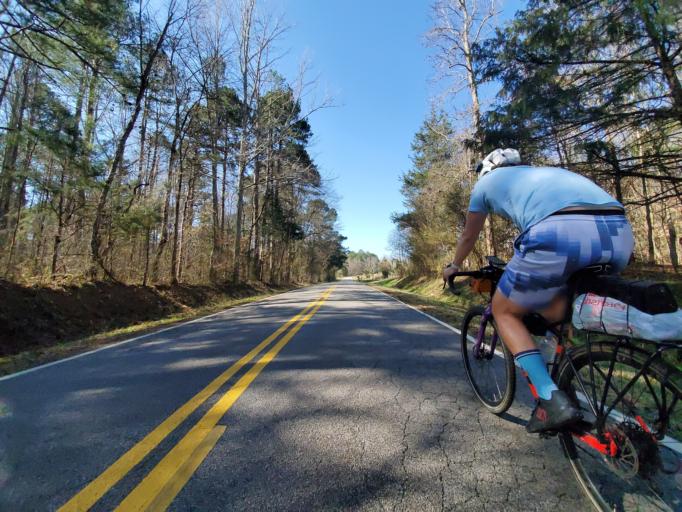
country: US
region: Georgia
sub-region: Clarke County
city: Country Club Estates
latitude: 34.0010
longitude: -83.4667
